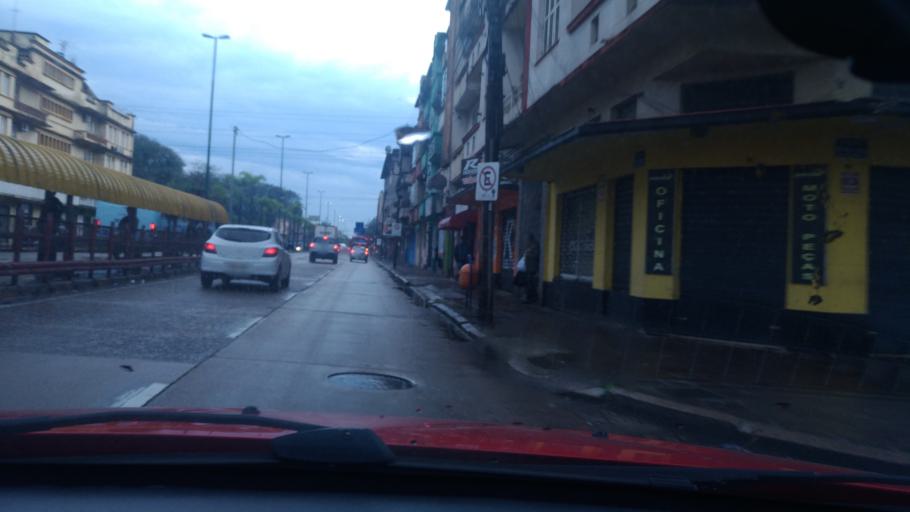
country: BR
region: Rio Grande do Sul
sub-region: Porto Alegre
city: Porto Alegre
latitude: -30.0071
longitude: -51.2013
